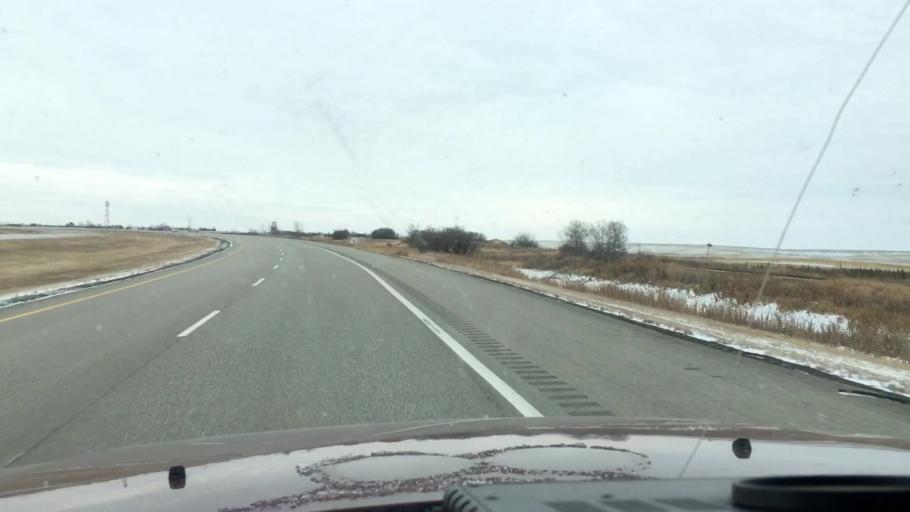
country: CA
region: Saskatchewan
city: Watrous
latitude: 51.3815
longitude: -106.1600
